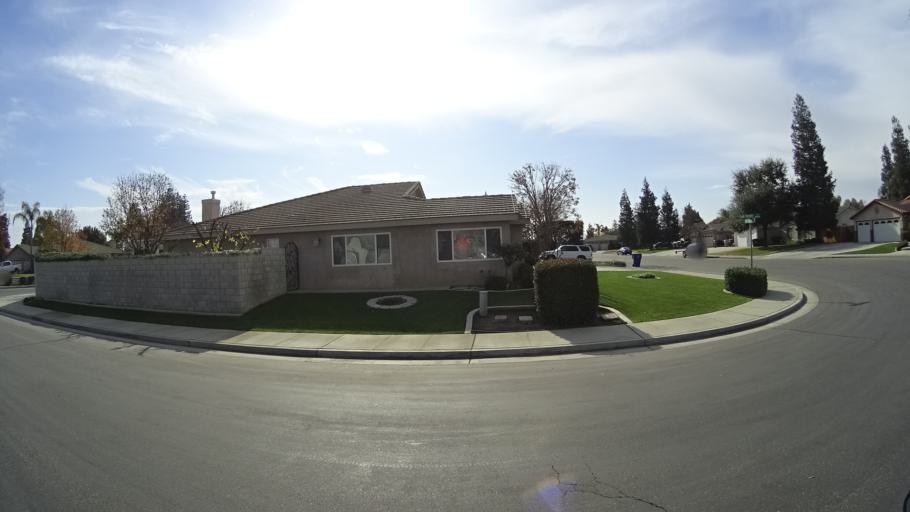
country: US
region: California
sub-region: Kern County
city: Greenacres
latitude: 35.4031
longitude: -119.0669
